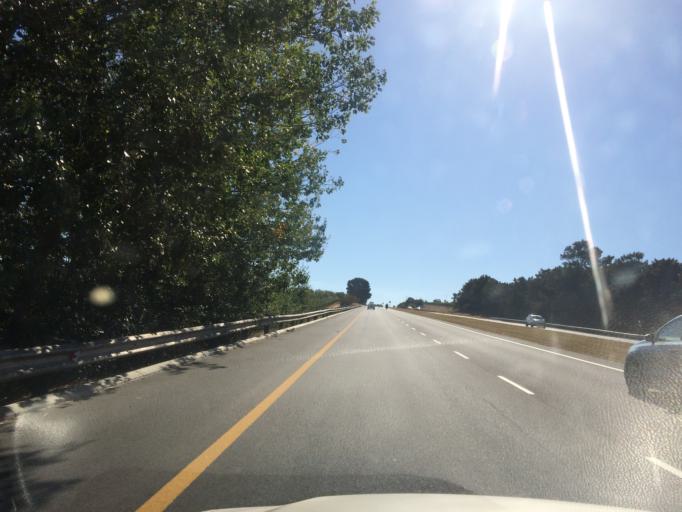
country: ZA
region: Western Cape
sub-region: City of Cape Town
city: Kraaifontein
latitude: -33.9630
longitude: 18.7403
